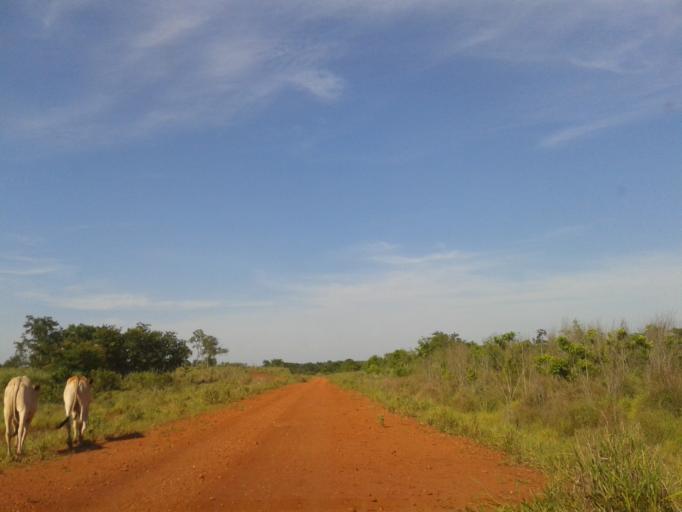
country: BR
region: Minas Gerais
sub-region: Santa Vitoria
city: Santa Vitoria
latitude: -19.1161
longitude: -50.5500
